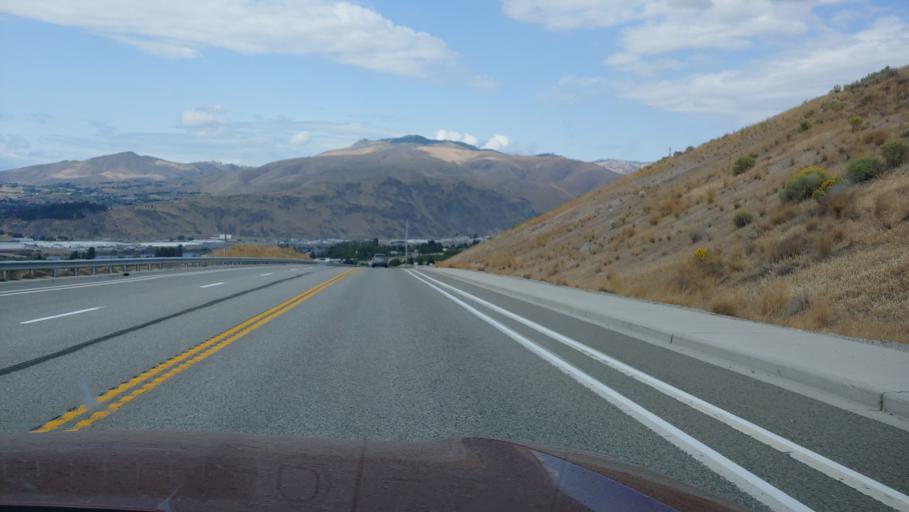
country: US
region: Washington
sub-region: Douglas County
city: East Wenatchee Bench
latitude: 47.4603
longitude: -120.2918
